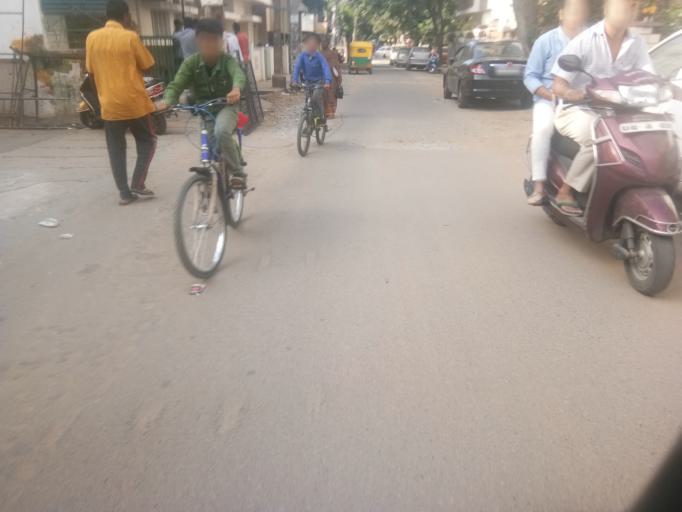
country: IN
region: Karnataka
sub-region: Bangalore Urban
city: Bangalore
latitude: 13.0051
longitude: 77.6007
